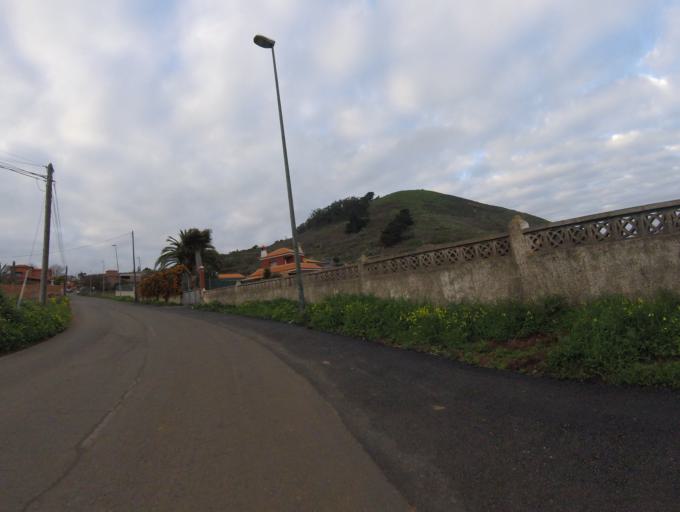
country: ES
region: Canary Islands
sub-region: Provincia de Santa Cruz de Tenerife
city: La Laguna
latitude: 28.4520
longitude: -16.3570
